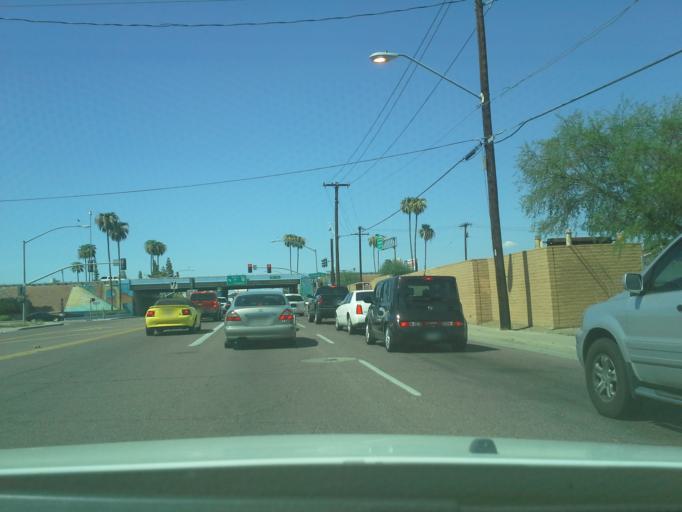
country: US
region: Arizona
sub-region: Maricopa County
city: Phoenix
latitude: 33.4276
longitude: -112.0651
